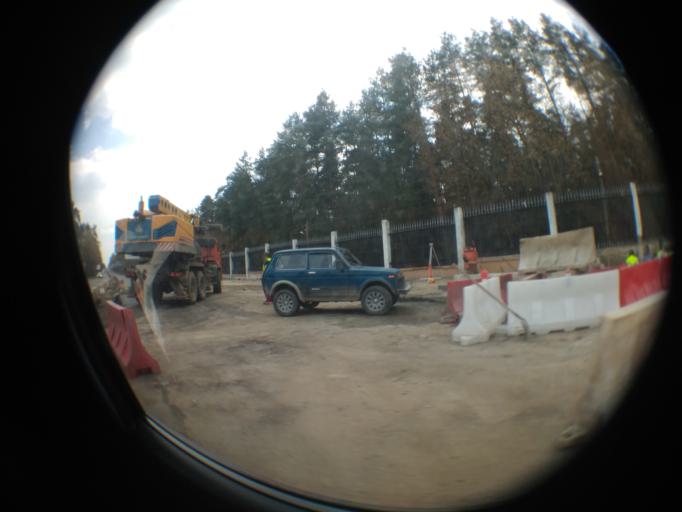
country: RU
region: Moskovskaya
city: Zhukovskiy
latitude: 55.5884
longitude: 38.1191
